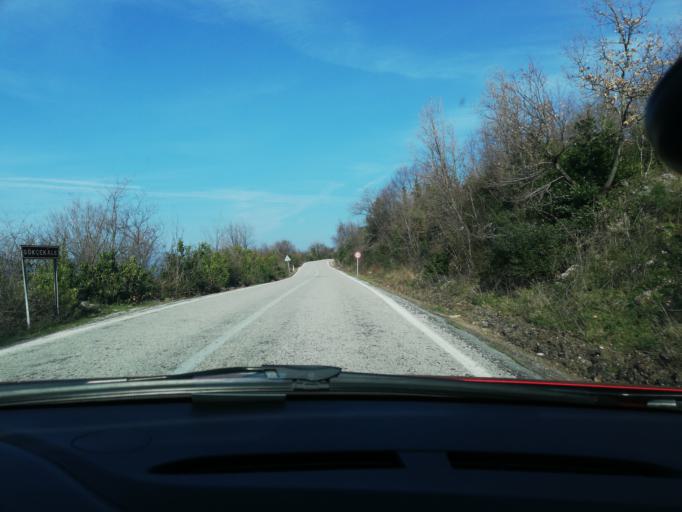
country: TR
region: Bartin
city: Kurucasile
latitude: 41.8566
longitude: 32.7790
